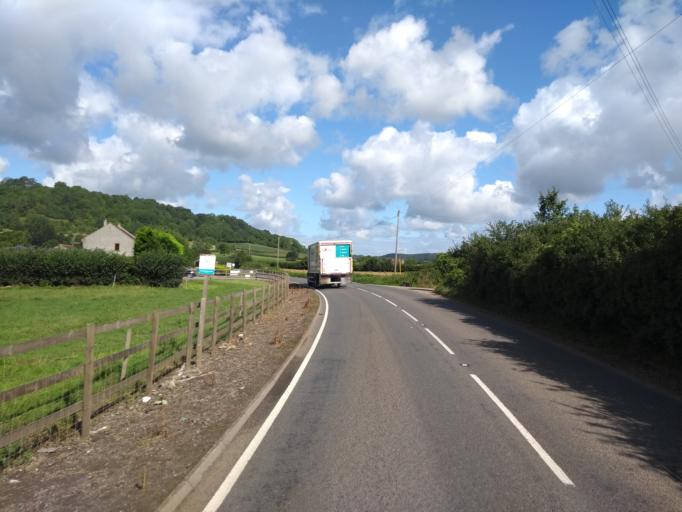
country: GB
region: England
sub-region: Somerset
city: Street
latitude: 51.0822
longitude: -2.7250
